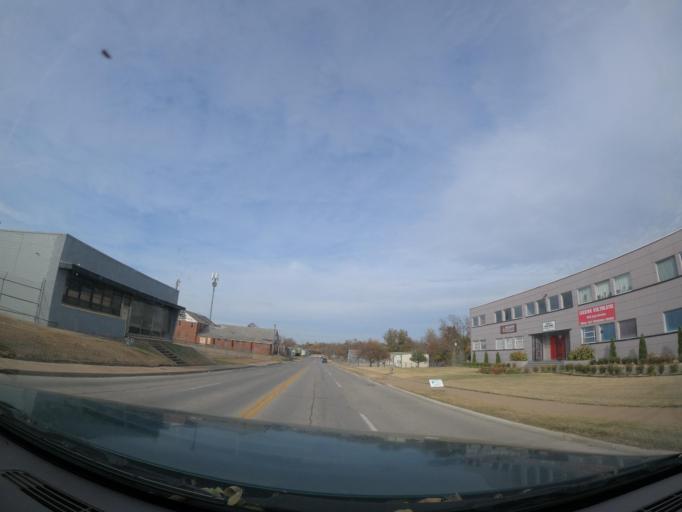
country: US
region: Oklahoma
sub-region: Tulsa County
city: Tulsa
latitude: 36.1746
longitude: -95.9672
